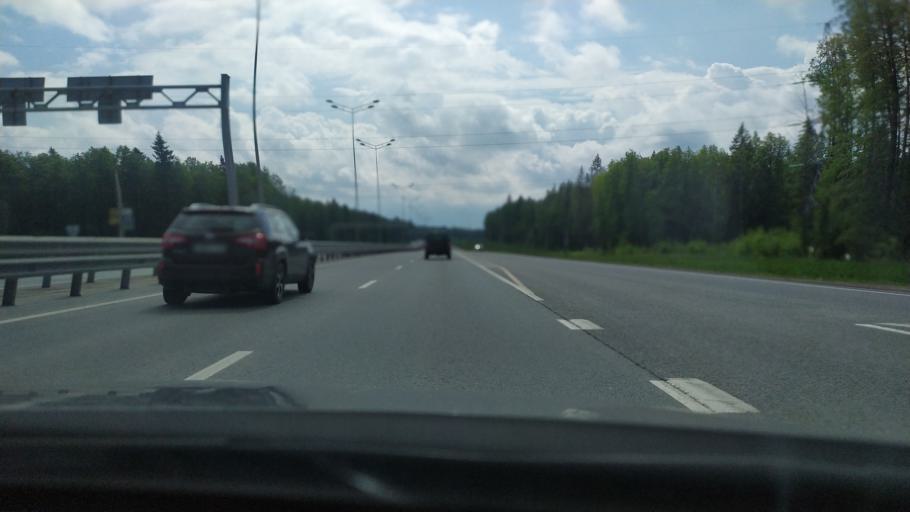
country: RU
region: Perm
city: Novyye Lyady
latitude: 58.0409
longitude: 56.4318
